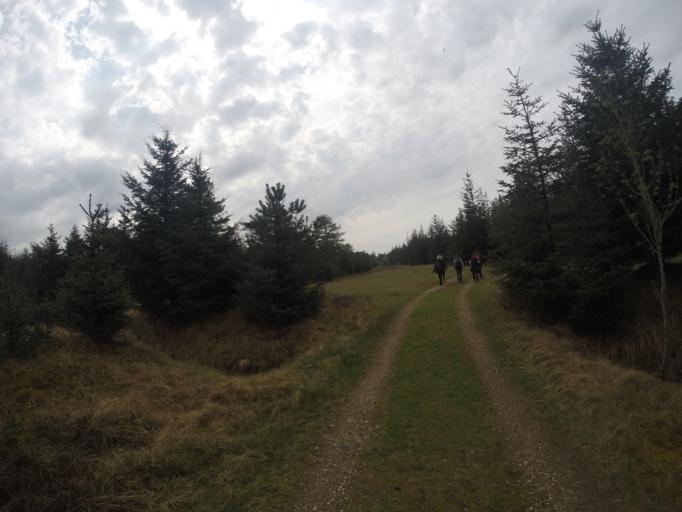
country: DK
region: North Denmark
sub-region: Thisted Kommune
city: Hanstholm
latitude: 57.0409
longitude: 8.5717
